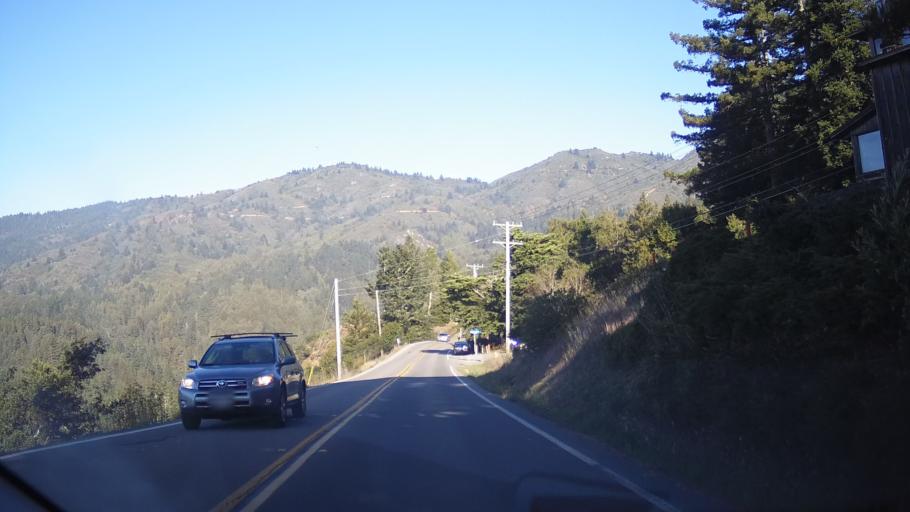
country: US
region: California
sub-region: Marin County
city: Mill Valley
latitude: 37.9065
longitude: -122.5741
